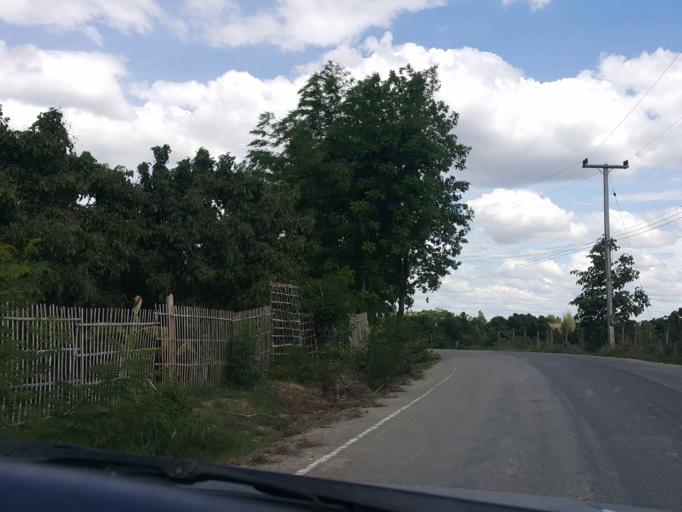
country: TH
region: Chiang Mai
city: Doi Lo
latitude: 18.4754
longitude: 98.7499
